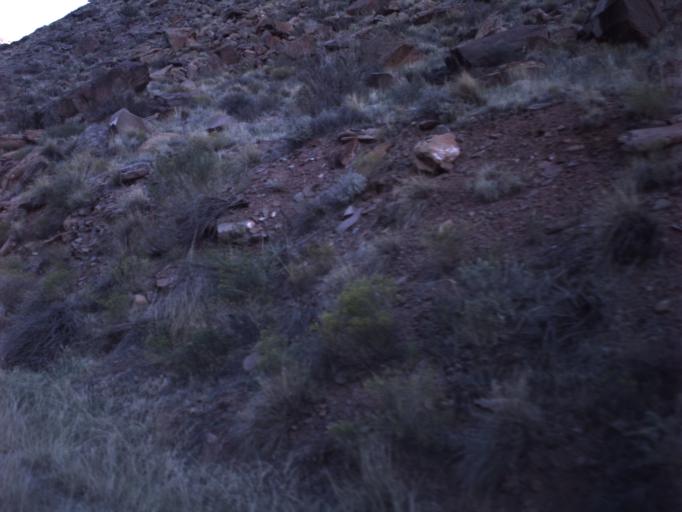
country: US
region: Utah
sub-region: Grand County
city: Moab
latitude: 38.6287
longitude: -109.5017
